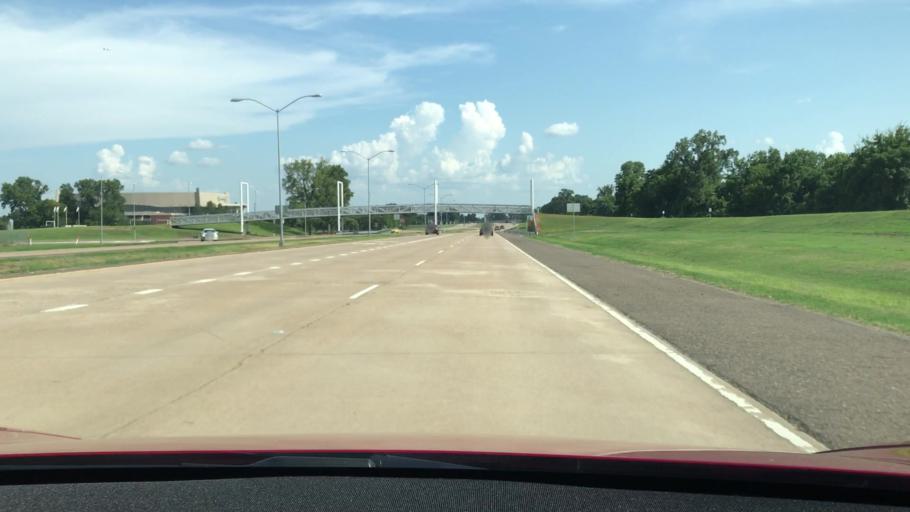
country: US
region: Louisiana
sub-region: Bossier Parish
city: Bossier City
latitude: 32.4710
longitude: -93.6780
